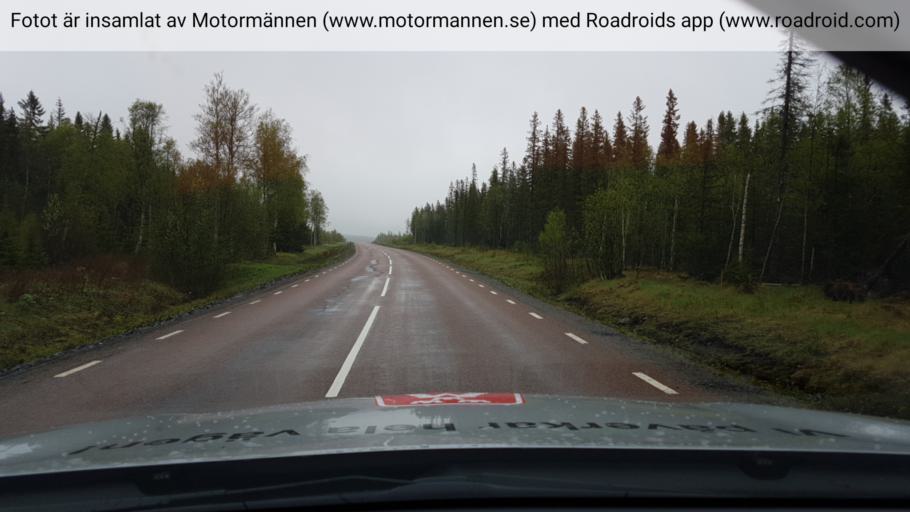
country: SE
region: Jaemtland
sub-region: Krokoms Kommun
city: Valla
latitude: 63.1385
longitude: 13.9431
